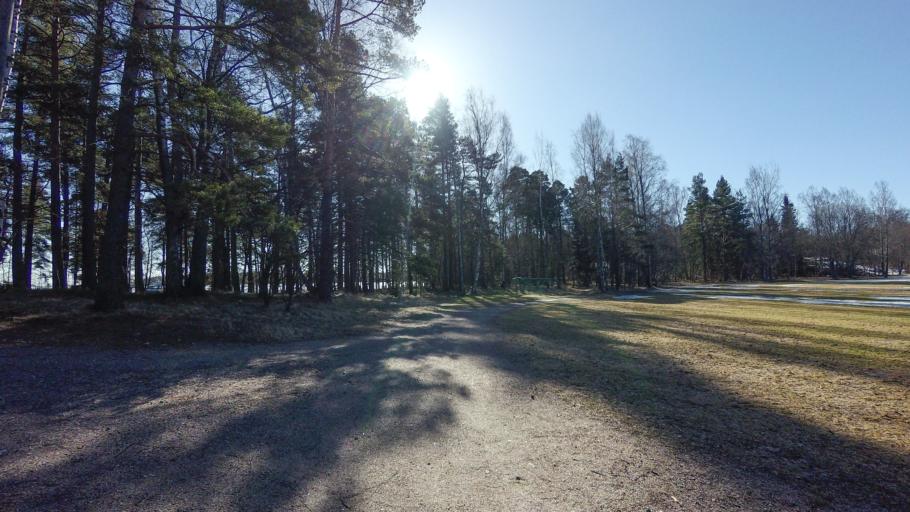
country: FI
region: Uusimaa
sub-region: Helsinki
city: Vantaa
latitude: 60.1770
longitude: 25.0616
